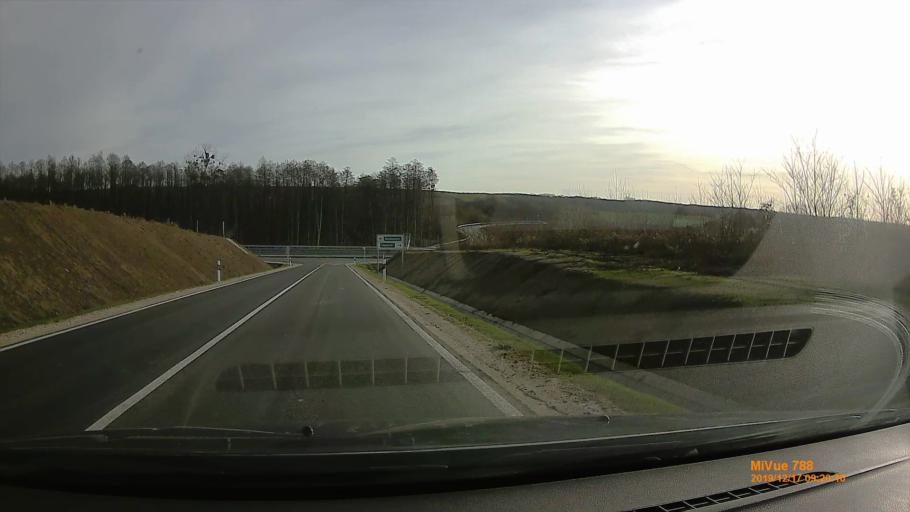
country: HU
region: Somogy
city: Karad
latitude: 46.5795
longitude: 17.8042
